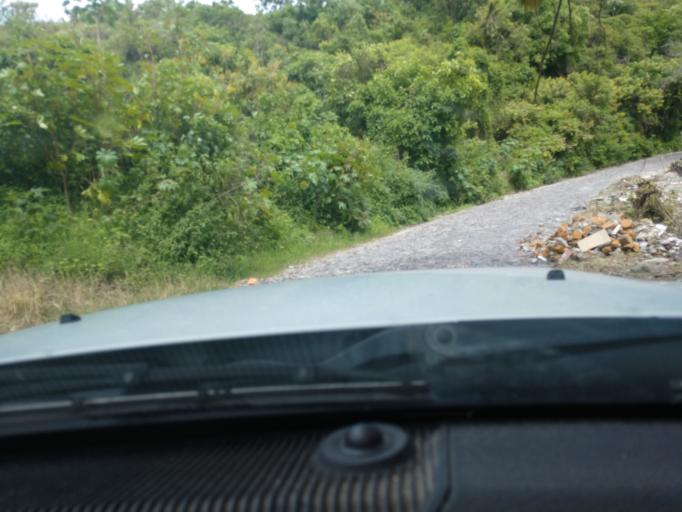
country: MX
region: Nayarit
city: Xalisco
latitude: 21.4425
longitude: -104.9115
